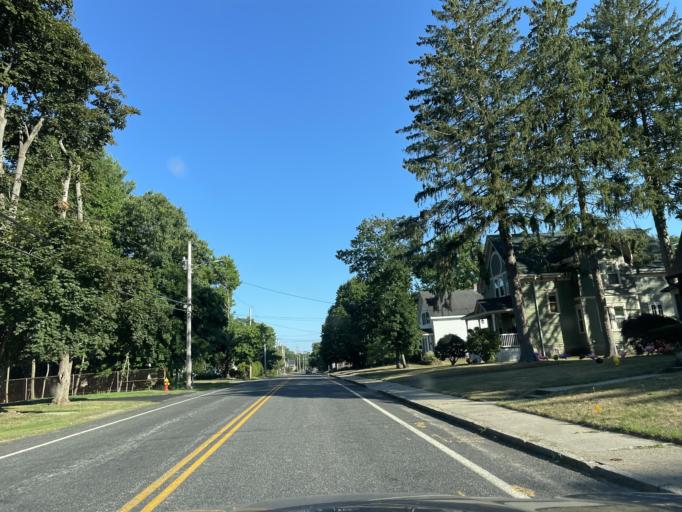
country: US
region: Massachusetts
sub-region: Bristol County
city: Mansfield
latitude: 42.0326
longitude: -71.2294
